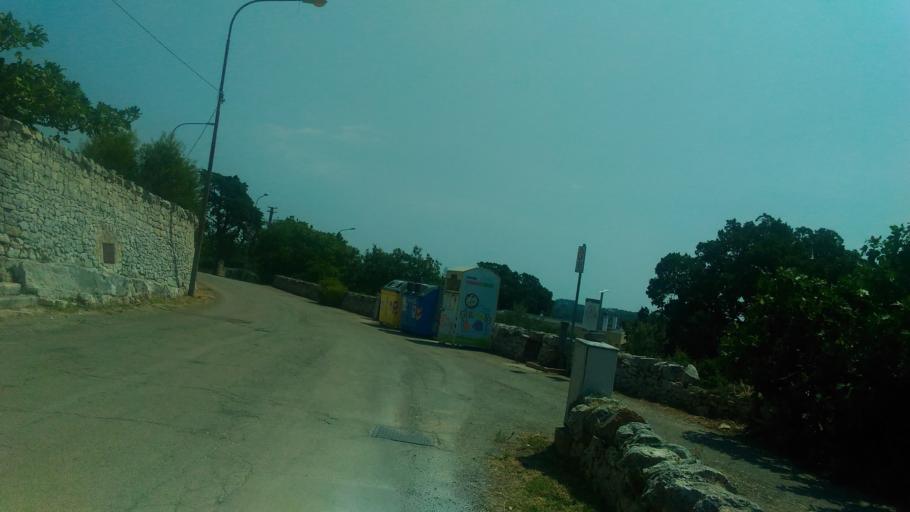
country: IT
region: Apulia
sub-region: Provincia di Brindisi
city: Cisternino
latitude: 40.7468
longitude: 17.3758
